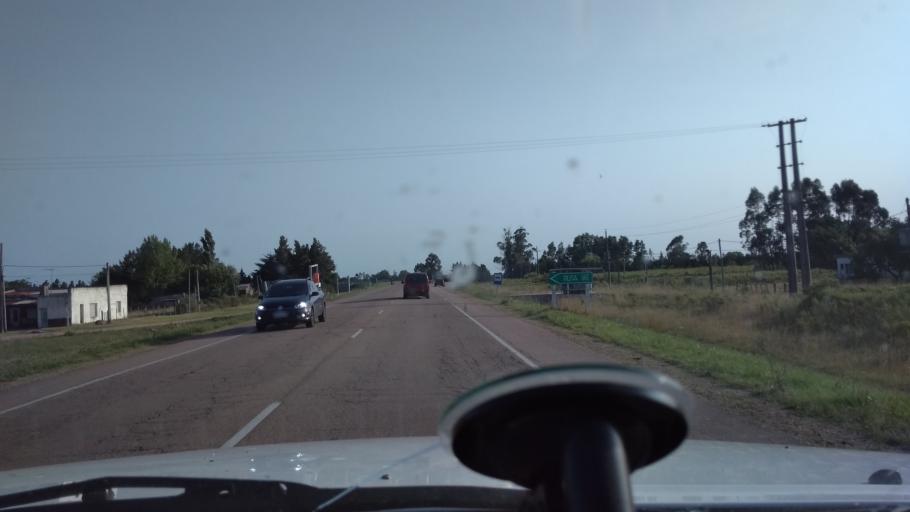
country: UY
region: Canelones
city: Sauce
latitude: -34.6361
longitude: -56.0524
